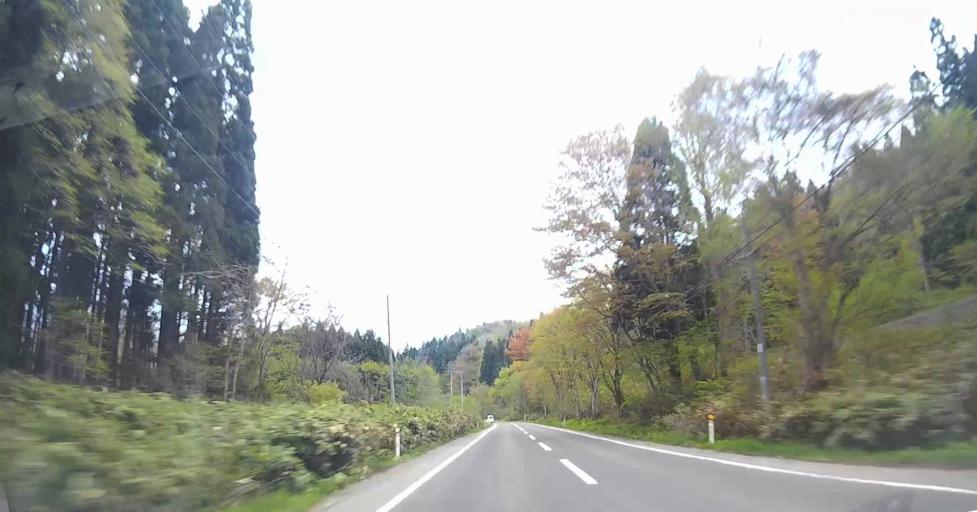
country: JP
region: Aomori
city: Goshogawara
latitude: 41.1270
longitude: 140.5196
